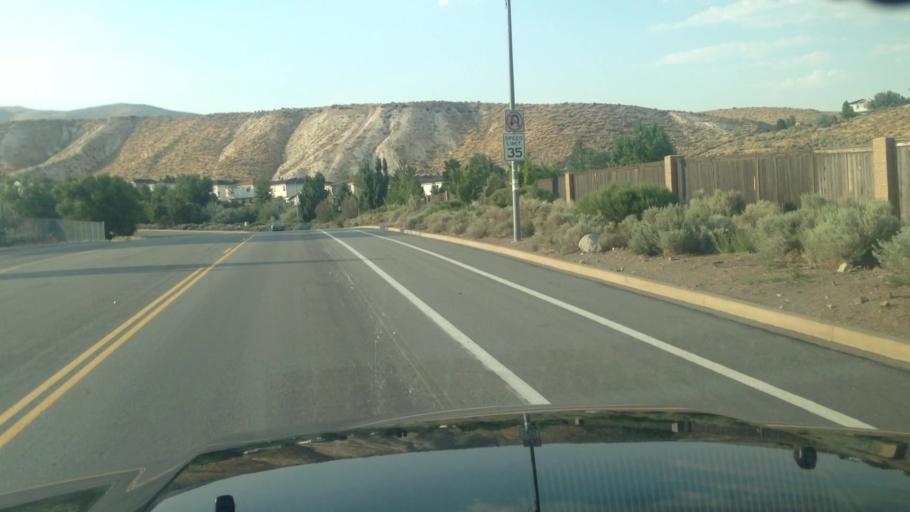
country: US
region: Nevada
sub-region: Washoe County
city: Mogul
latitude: 39.5361
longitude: -119.8819
